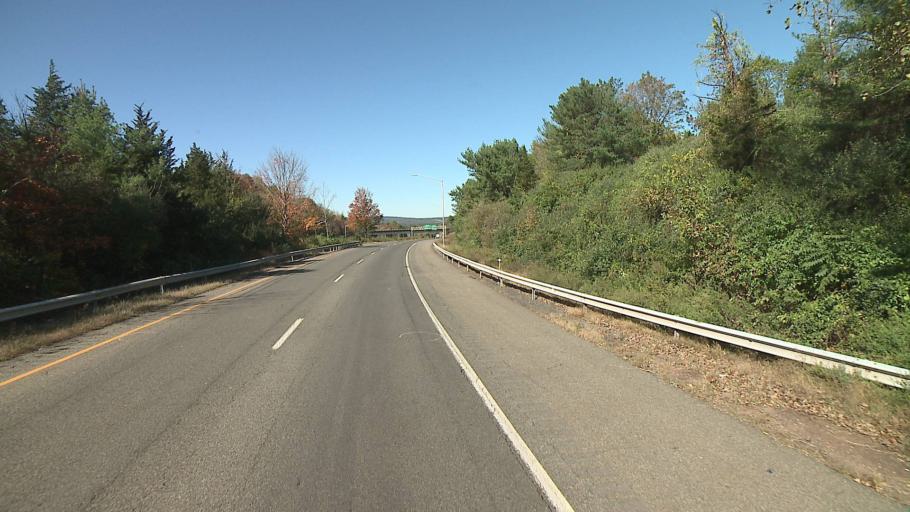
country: US
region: Connecticut
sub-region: New Haven County
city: Meriden
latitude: 41.5296
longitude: -72.7496
